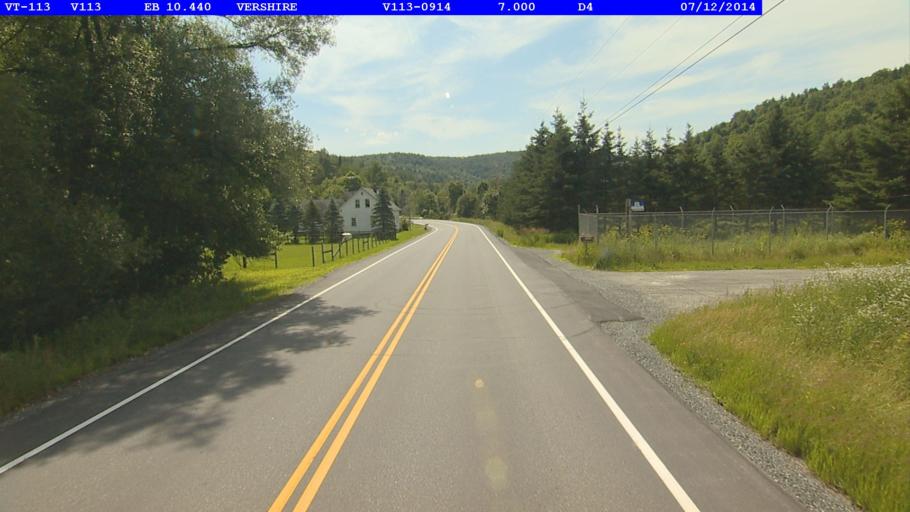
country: US
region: New Hampshire
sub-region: Grafton County
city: Orford
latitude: 43.9454
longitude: -72.2718
